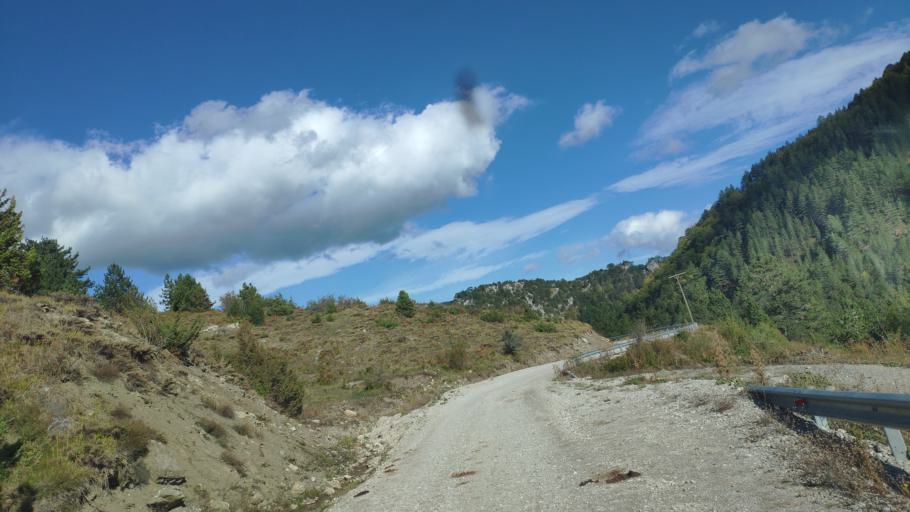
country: AL
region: Korce
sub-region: Rrethi i Devollit
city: Miras
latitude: 40.4027
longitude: 20.8525
